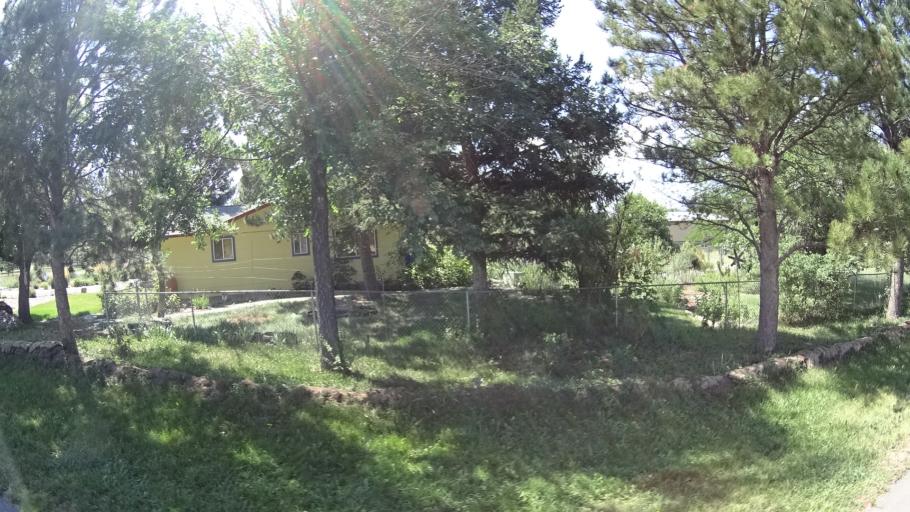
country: US
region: Colorado
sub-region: El Paso County
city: Air Force Academy
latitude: 38.9396
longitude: -104.7921
